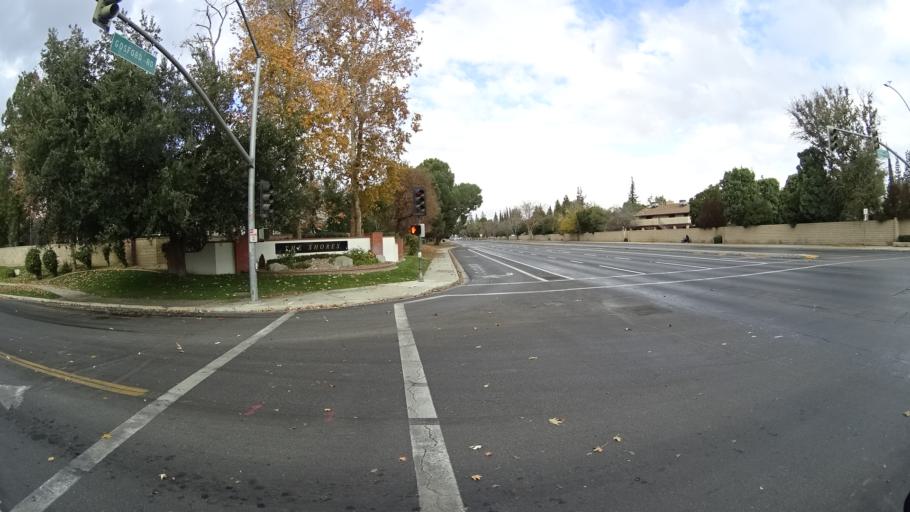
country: US
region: California
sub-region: Kern County
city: Greenacres
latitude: 35.3497
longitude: -119.0924
